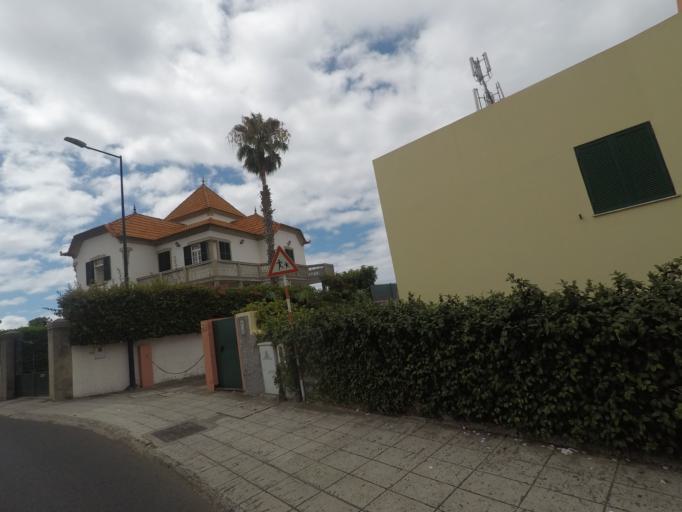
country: PT
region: Madeira
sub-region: Funchal
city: Funchal
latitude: 32.6494
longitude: -16.8936
